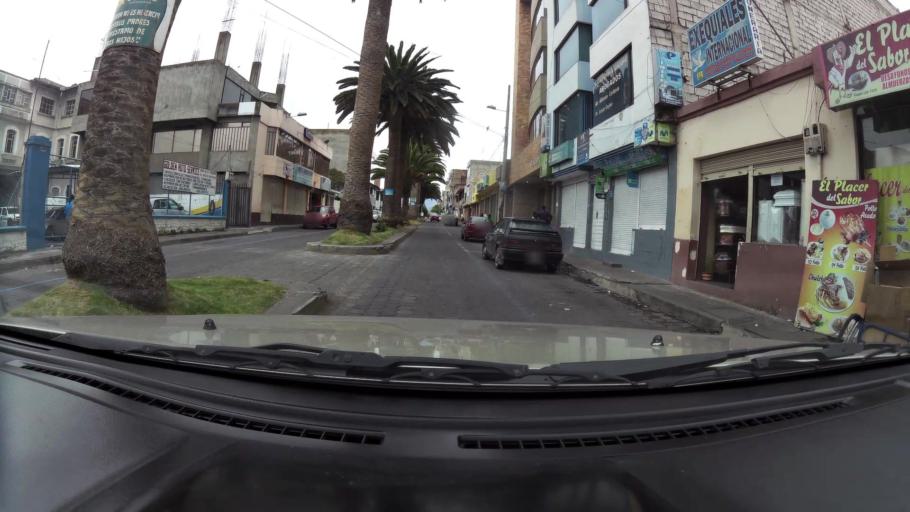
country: EC
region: Cotopaxi
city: Latacunga
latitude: -0.9296
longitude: -78.6089
